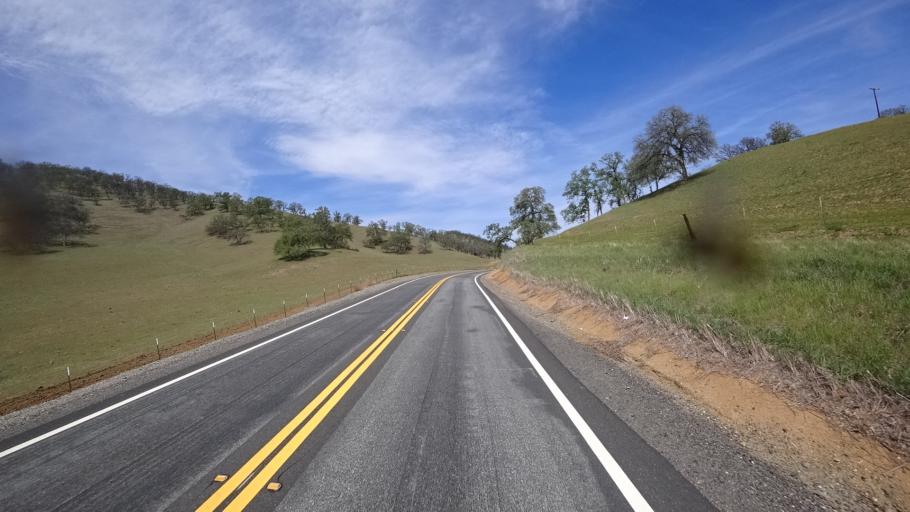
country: US
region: California
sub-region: Glenn County
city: Willows
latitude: 39.5964
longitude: -122.4660
